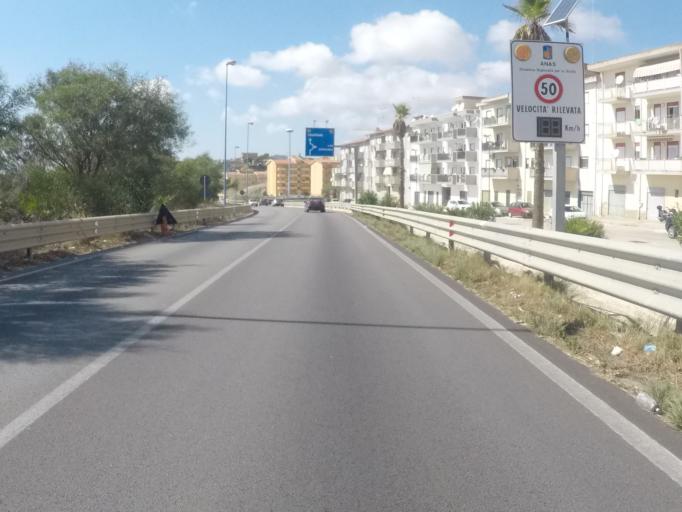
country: IT
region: Sicily
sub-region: Agrigento
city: Porto Empedocle
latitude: 37.2924
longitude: 13.5148
